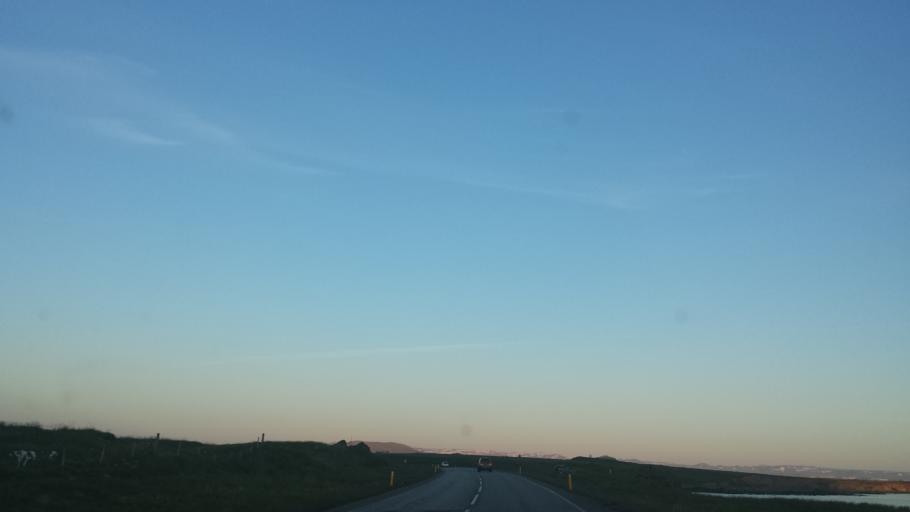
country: IS
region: Capital Region
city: Reykjavik
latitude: 64.2275
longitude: -21.8143
